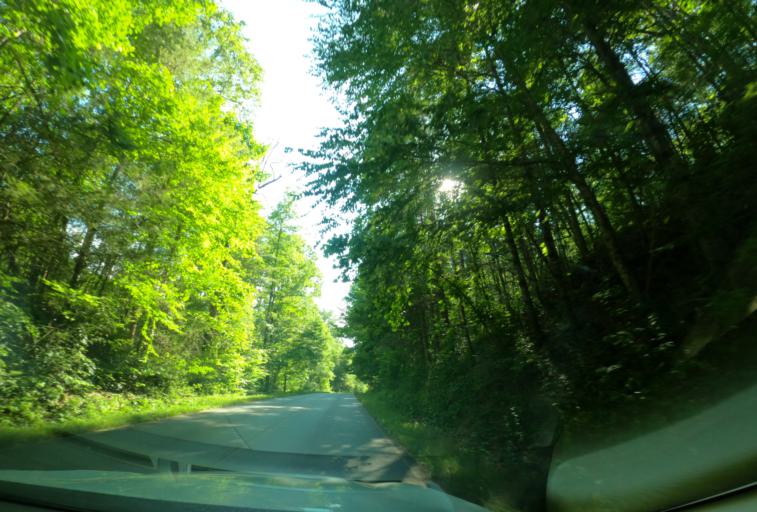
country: US
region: North Carolina
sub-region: Transylvania County
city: Brevard
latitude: 35.2860
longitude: -82.7878
